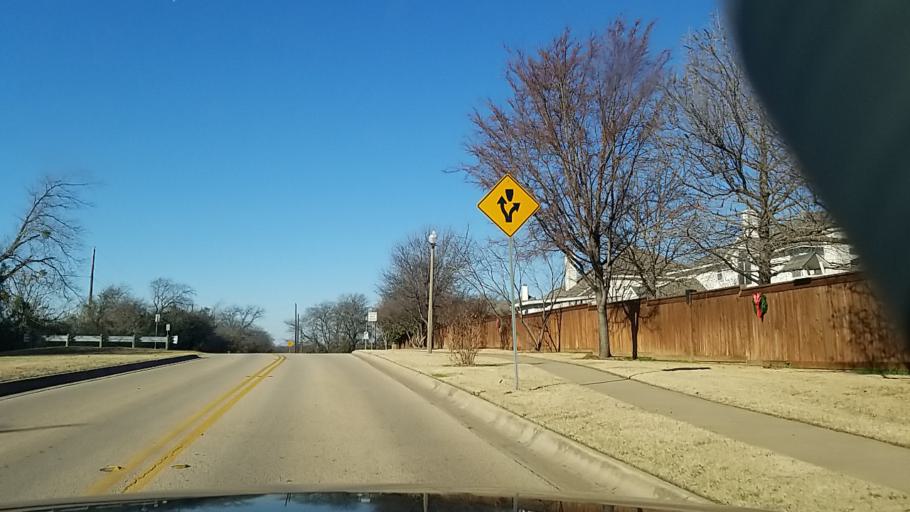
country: US
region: Texas
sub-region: Denton County
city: Copper Canyon
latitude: 33.1472
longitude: -97.1259
